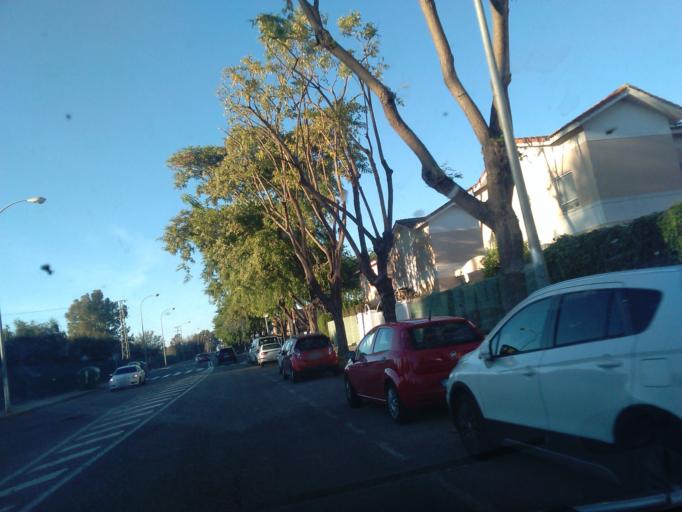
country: ES
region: Andalusia
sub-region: Provincia de Sevilla
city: Sevilla
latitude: 37.3936
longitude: -5.9275
